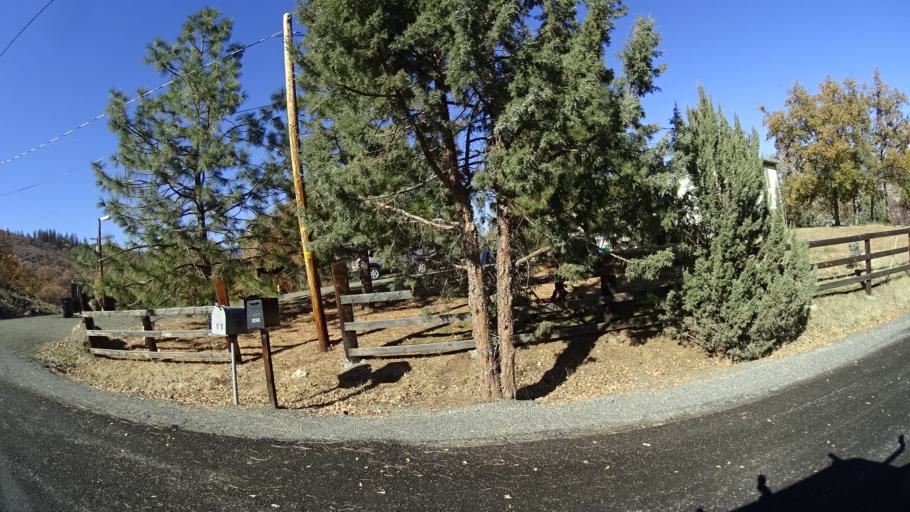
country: US
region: California
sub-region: Siskiyou County
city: Montague
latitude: 41.8791
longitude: -122.4926
